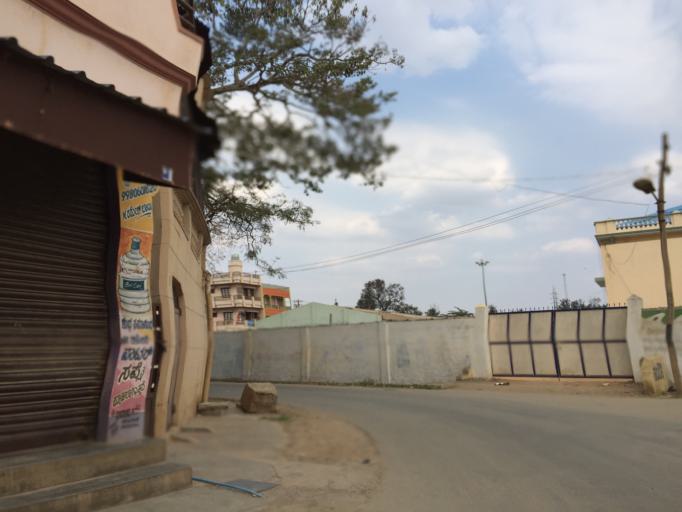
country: IN
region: Karnataka
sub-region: Chikkaballapur
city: Chik Ballapur
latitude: 13.4280
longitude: 77.7293
